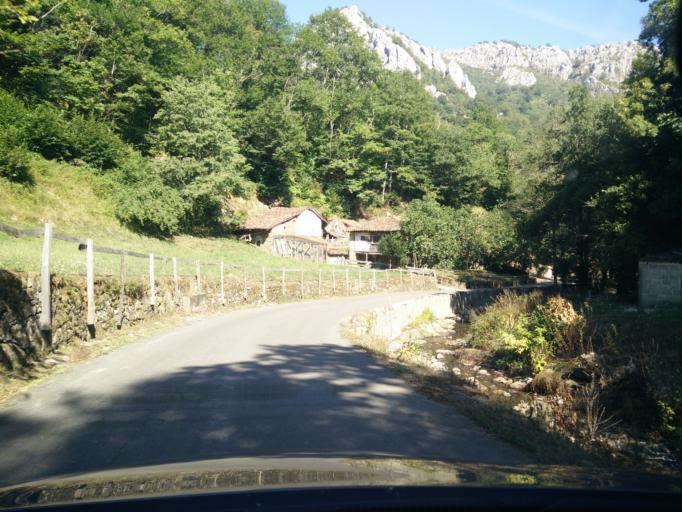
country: ES
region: Asturias
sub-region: Province of Asturias
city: Campo de Caso
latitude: 43.1550
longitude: -5.3928
